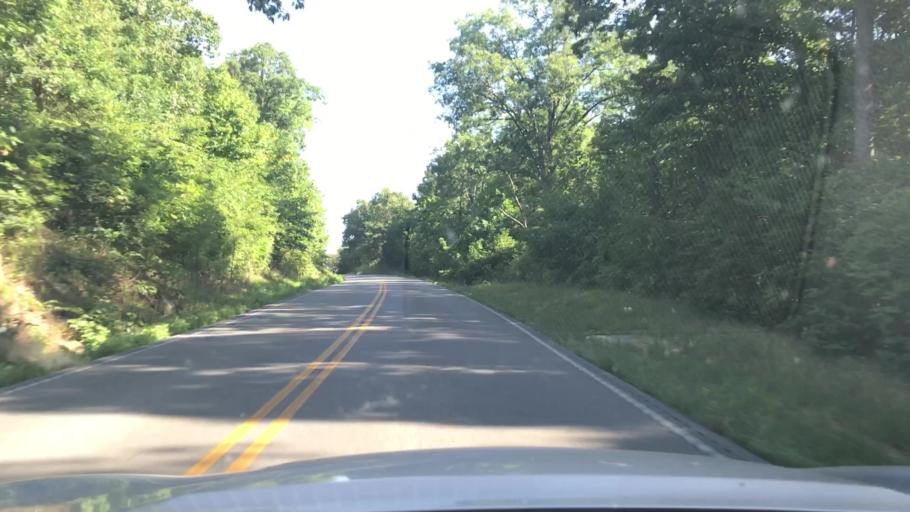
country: US
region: Kentucky
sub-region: Muhlenberg County
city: Greenville
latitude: 37.1120
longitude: -87.1276
